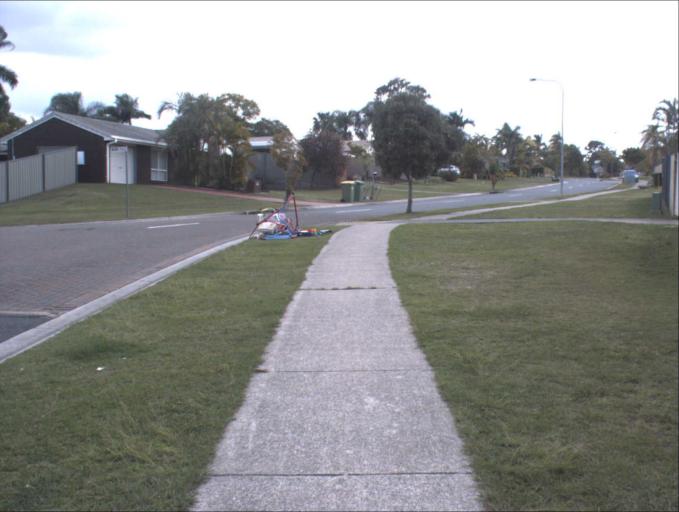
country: AU
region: Queensland
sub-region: Logan
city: Park Ridge South
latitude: -27.6955
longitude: 153.0173
